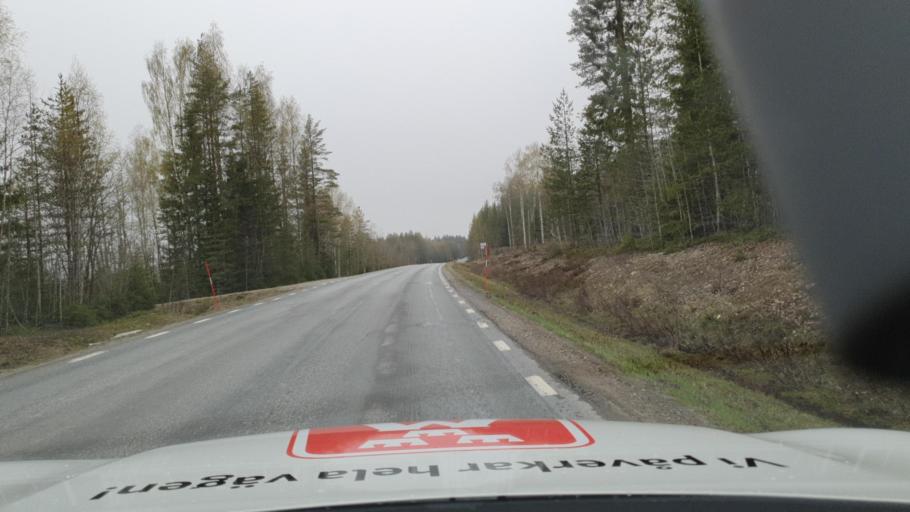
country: SE
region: Vaesterbotten
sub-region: Vannas Kommun
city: Vaennaes
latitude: 63.7713
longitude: 19.7093
